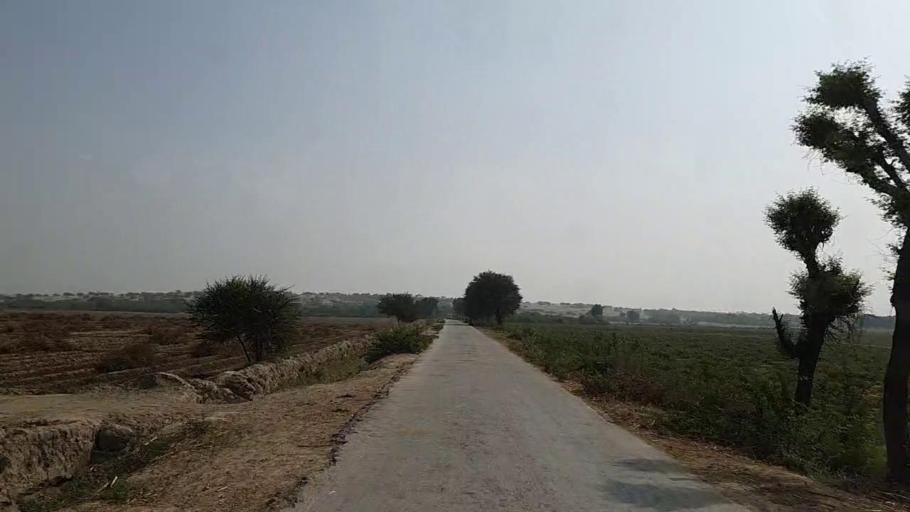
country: PK
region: Sindh
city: Naukot
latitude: 24.7504
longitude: 69.3472
